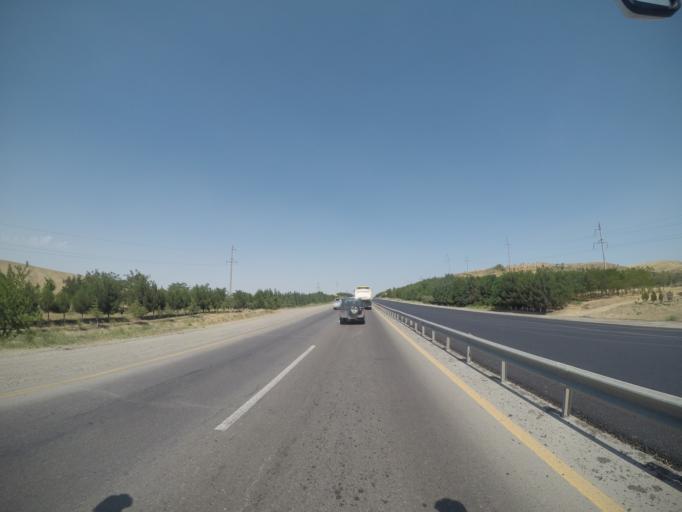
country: AZ
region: Haciqabul
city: Haciqabul
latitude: 40.0445
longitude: 48.9721
